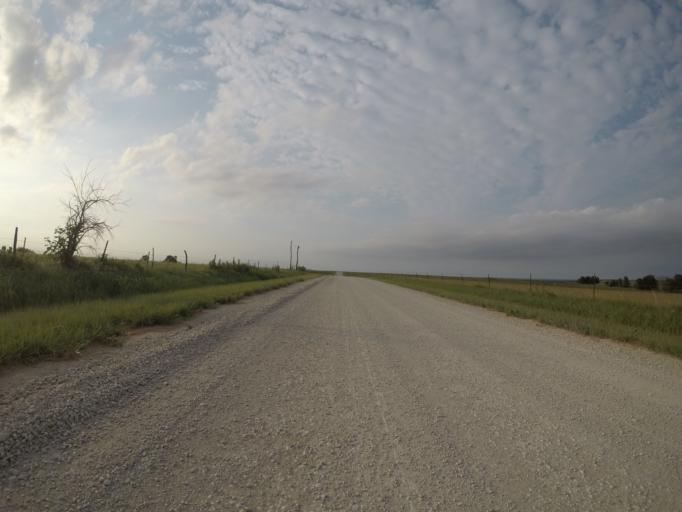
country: US
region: Kansas
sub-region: Pottawatomie County
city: Wamego
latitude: 39.1070
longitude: -96.3456
